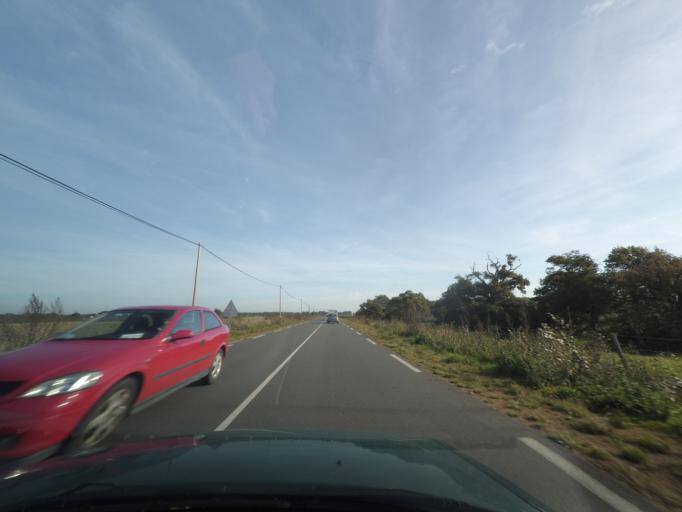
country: FR
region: Pays de la Loire
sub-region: Departement de la Vendee
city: Tiffauges
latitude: 47.0240
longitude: -1.1031
